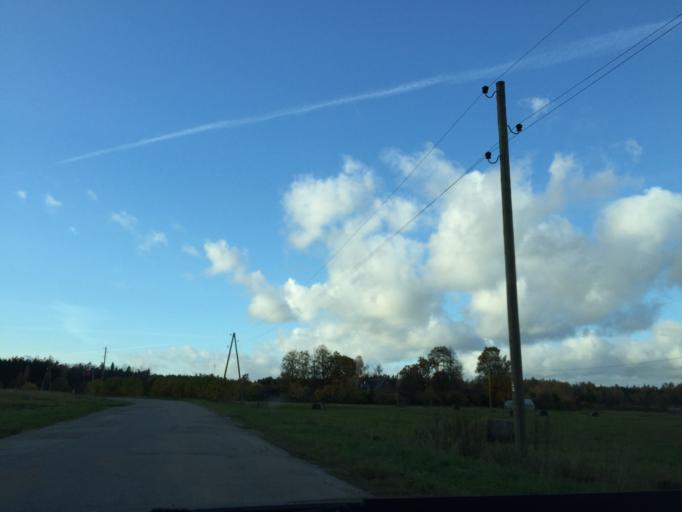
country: LV
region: Ogre
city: Jumprava
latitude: 56.7658
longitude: 25.0184
